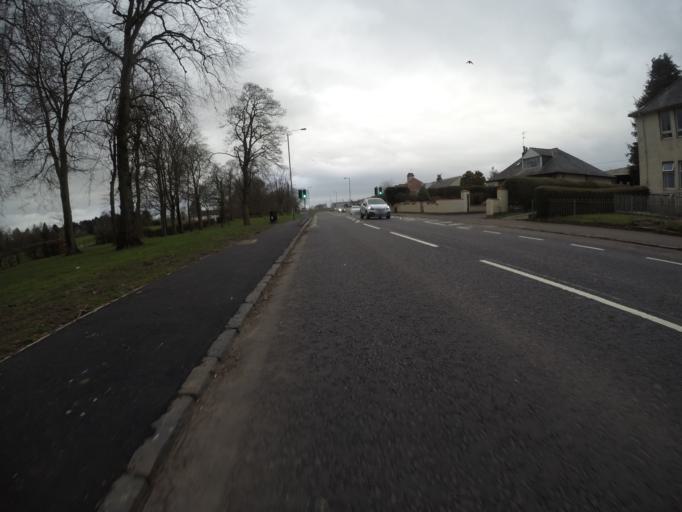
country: GB
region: Scotland
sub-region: East Ayrshire
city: Kilmarnock
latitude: 55.6113
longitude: -4.5210
